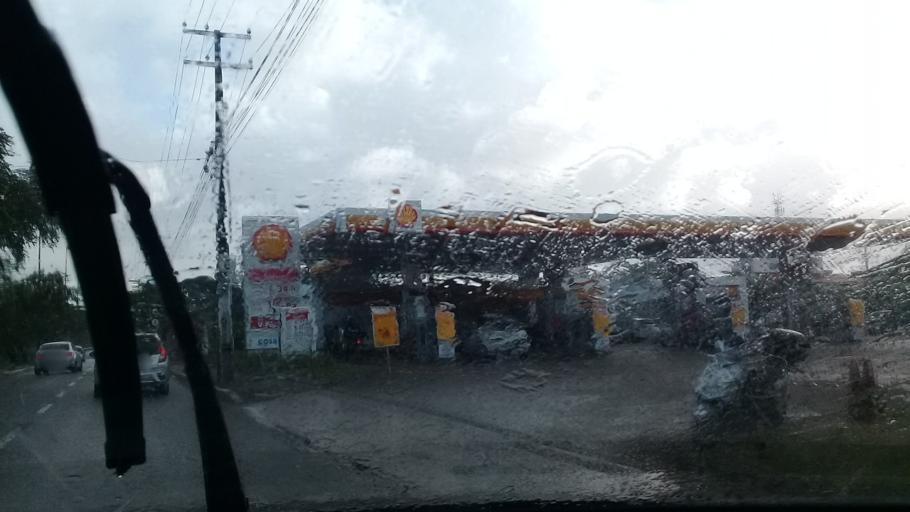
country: BR
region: Pernambuco
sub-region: Recife
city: Recife
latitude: -8.1304
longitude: -34.9108
